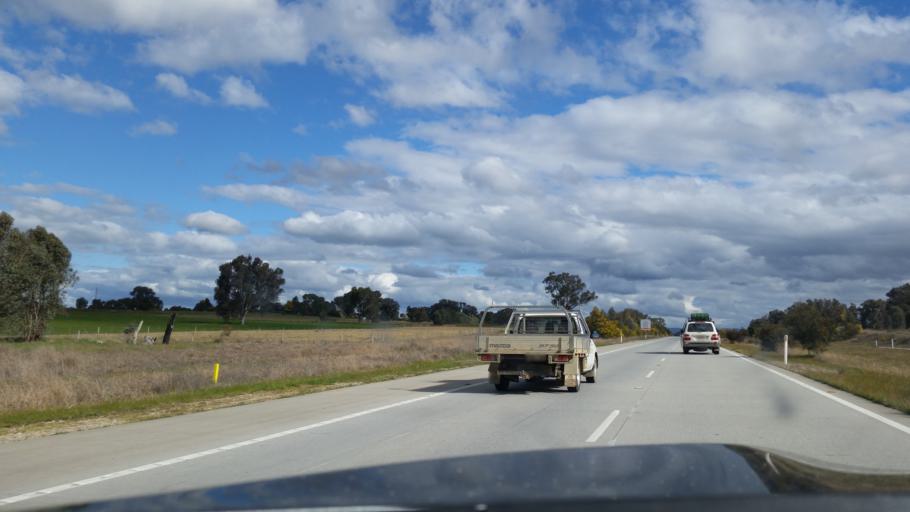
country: AU
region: New South Wales
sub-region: Albury Municipality
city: Lavington
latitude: -36.0065
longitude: 146.9902
